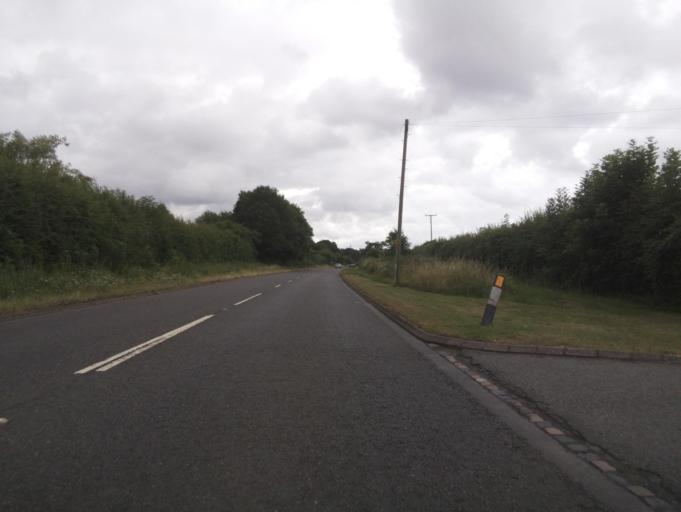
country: GB
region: England
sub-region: Worcestershire
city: Fernhill Heath
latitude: 52.2253
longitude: -2.1661
